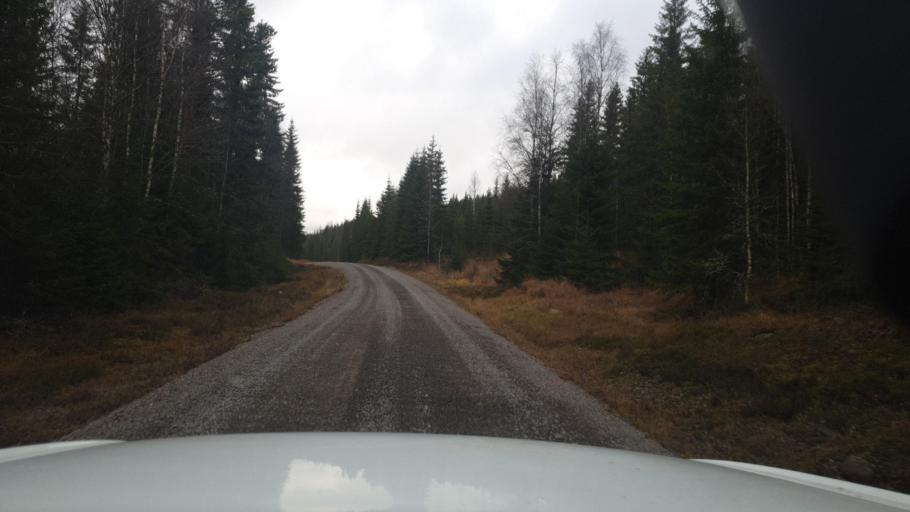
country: SE
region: Vaermland
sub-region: Eda Kommun
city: Charlottenberg
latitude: 60.0980
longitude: 12.6102
